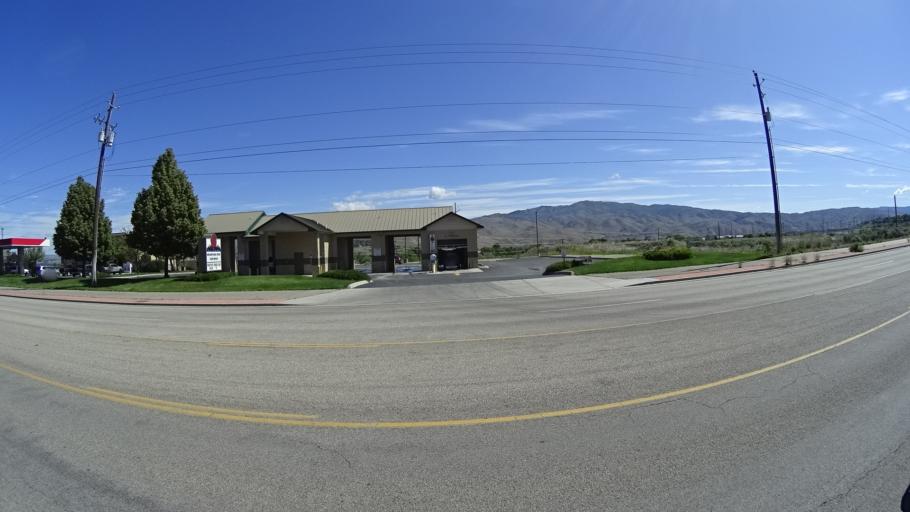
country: US
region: Idaho
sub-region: Ada County
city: Boise
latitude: 43.5593
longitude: -116.1665
